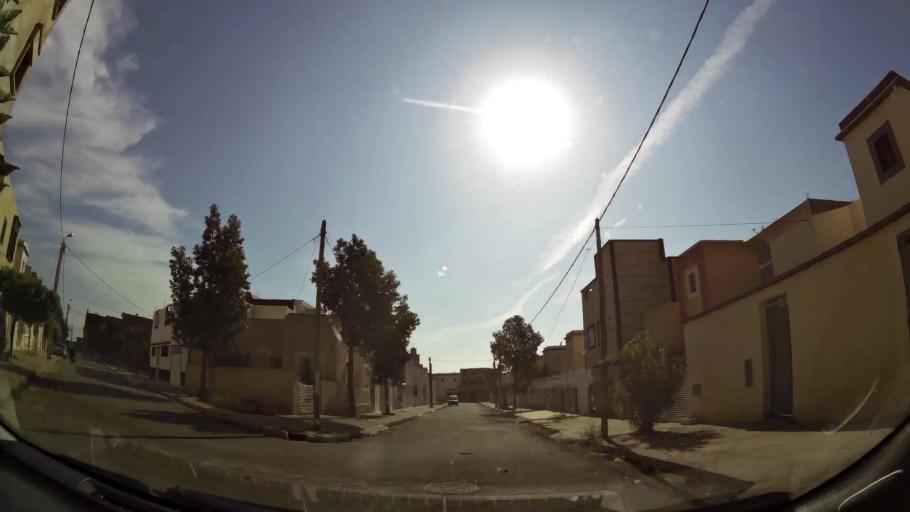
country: MA
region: Oriental
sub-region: Oujda-Angad
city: Oujda
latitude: 34.7194
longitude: -1.8826
